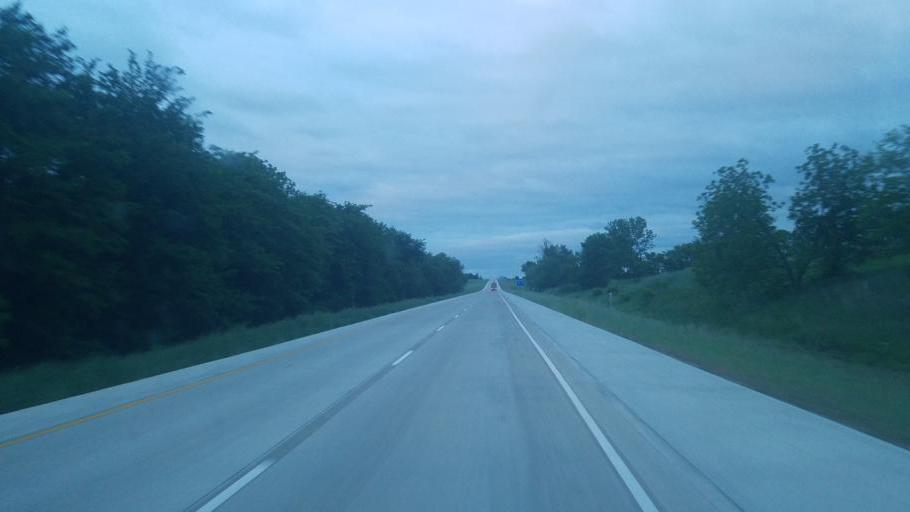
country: US
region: Iowa
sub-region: Decatur County
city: Lamoni
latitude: 40.6063
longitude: -93.9030
